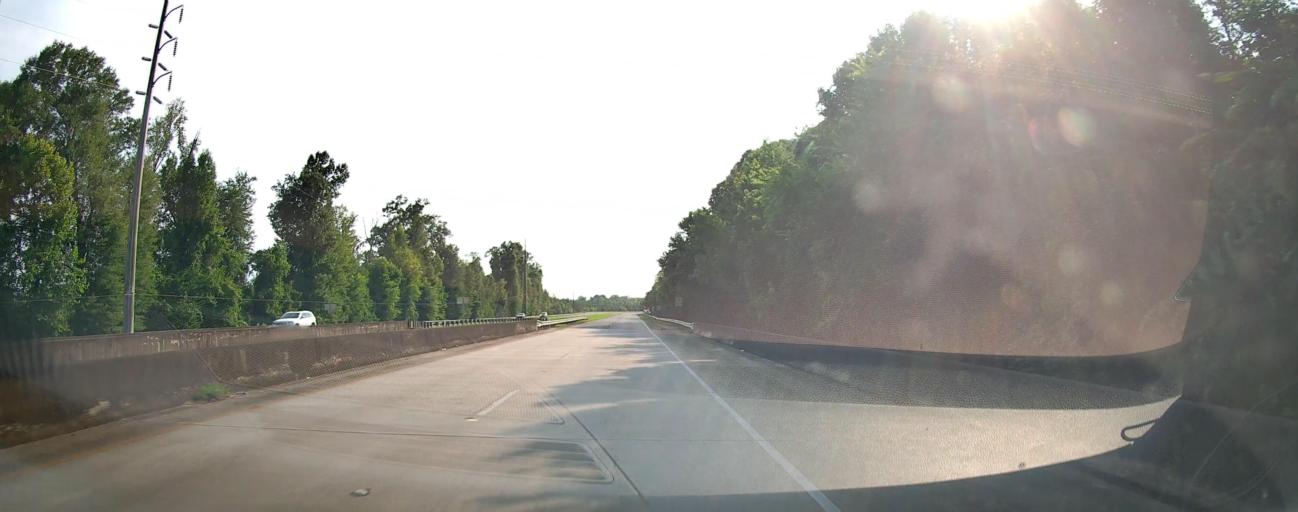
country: US
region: Georgia
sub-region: Taylor County
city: Reynolds
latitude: 32.5424
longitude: -84.0176
